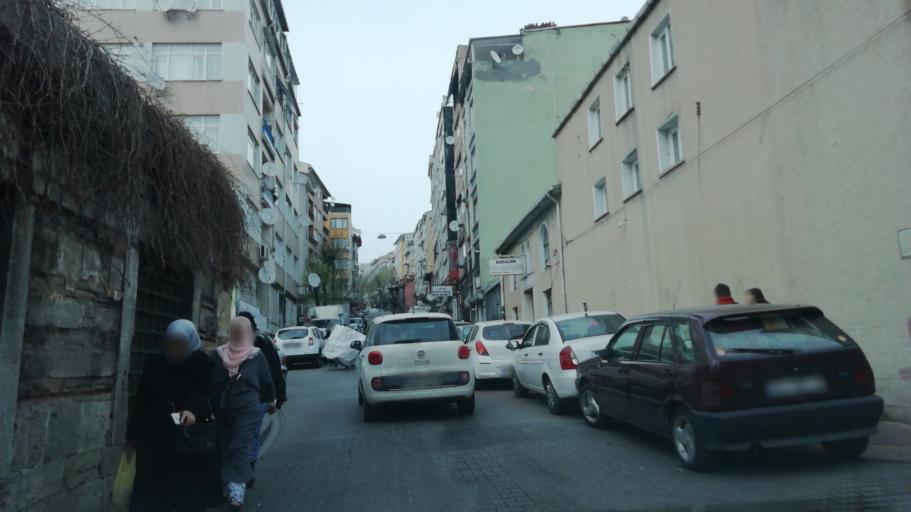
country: TR
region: Istanbul
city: Istanbul
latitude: 41.0133
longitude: 28.9485
